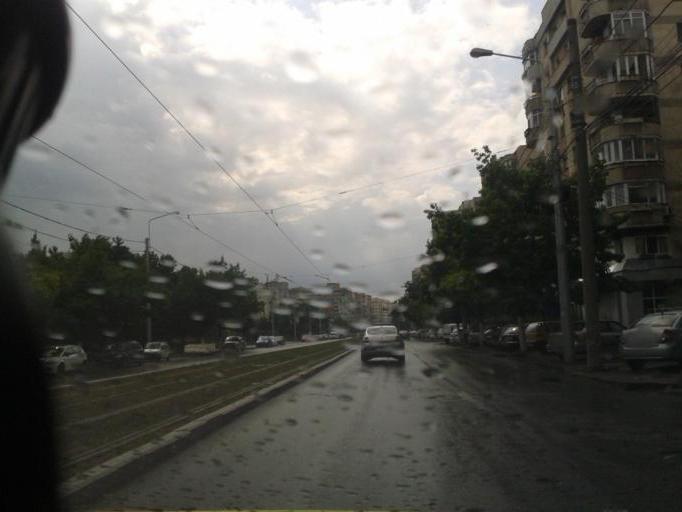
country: RO
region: Prahova
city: Ploiesti
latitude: 44.9468
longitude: 26.0149
